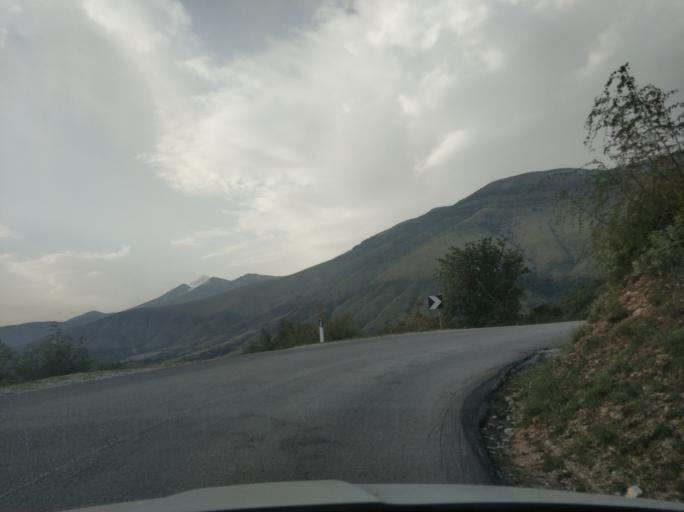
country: AL
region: Vlore
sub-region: Rrethi i Sarandes
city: Dhiver
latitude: 39.9237
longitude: 20.2025
